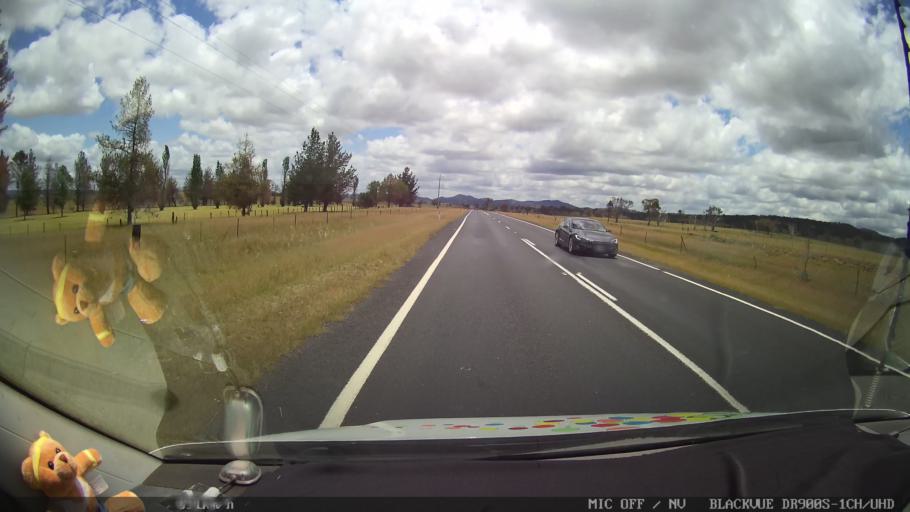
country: AU
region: New South Wales
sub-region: Glen Innes Severn
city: Glen Innes
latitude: -29.4286
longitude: 151.8565
